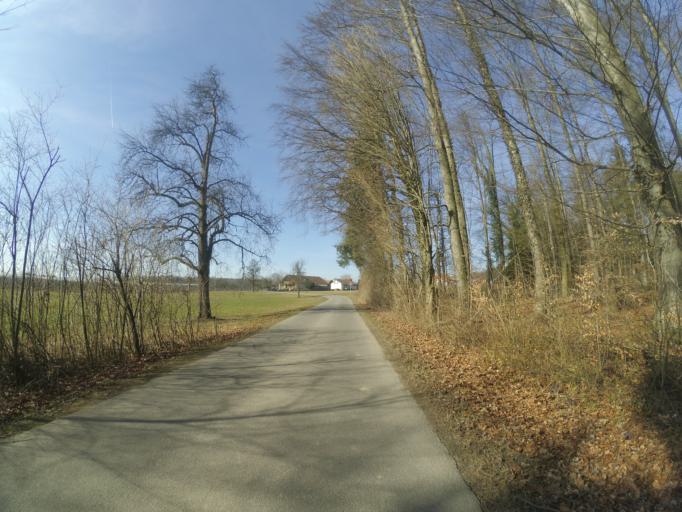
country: DE
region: Baden-Wuerttemberg
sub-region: Tuebingen Region
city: Meckenbeuren
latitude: 47.7196
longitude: 9.5724
